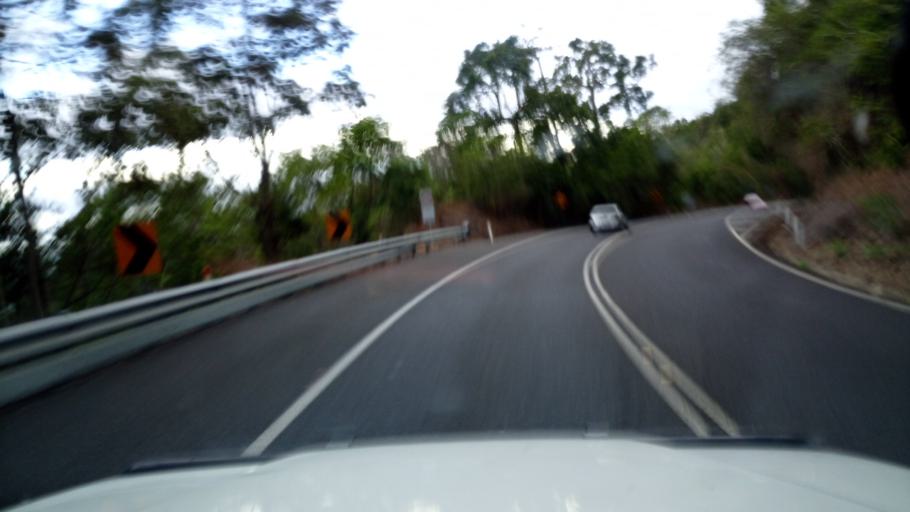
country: AU
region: Queensland
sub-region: Cairns
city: Redlynch
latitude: -16.8477
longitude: 145.6809
